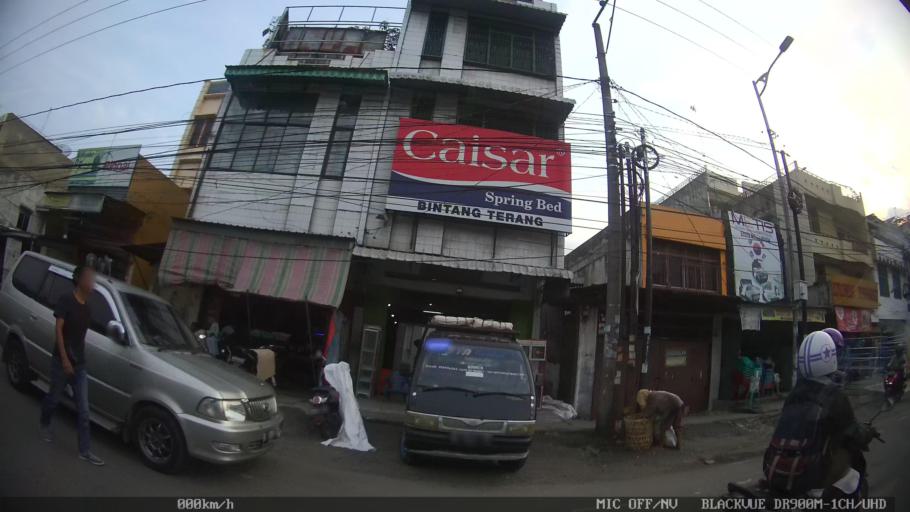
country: ID
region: North Sumatra
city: Sunggal
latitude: 3.5984
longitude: 98.6078
